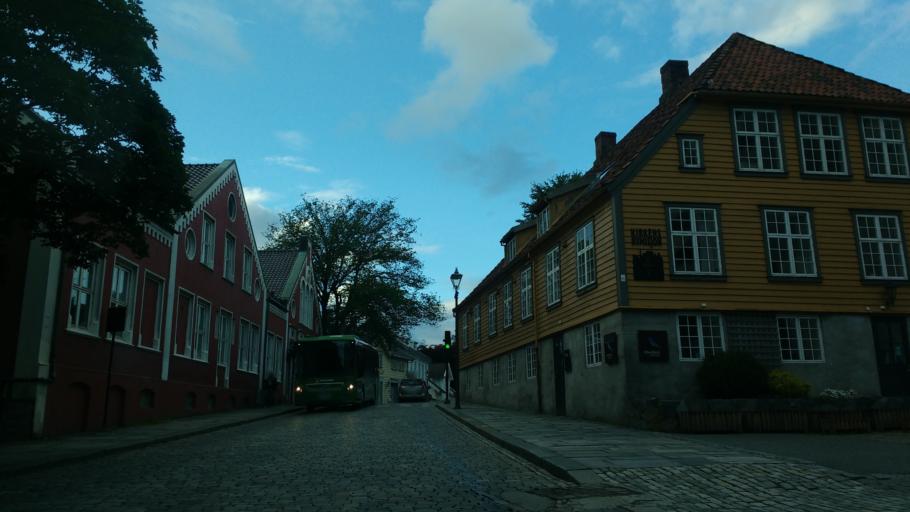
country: NO
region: Rogaland
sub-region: Stavanger
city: Stavanger
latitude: 58.9671
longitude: 5.7346
